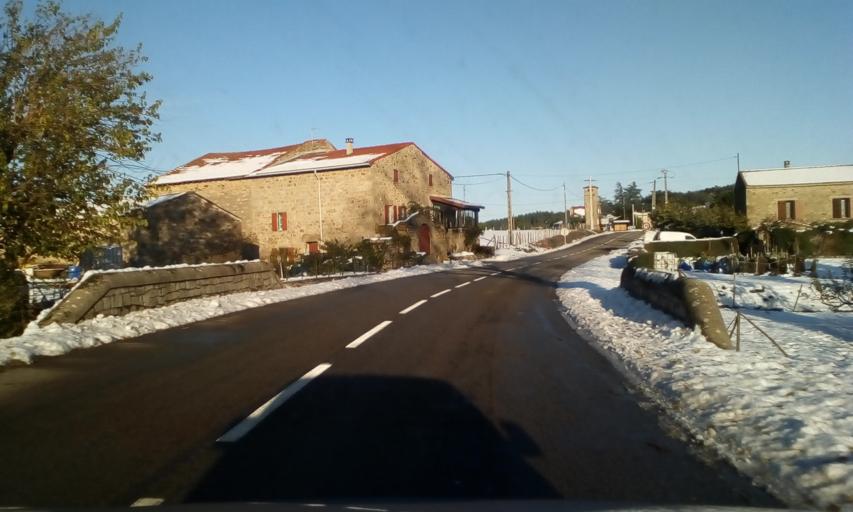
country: FR
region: Rhone-Alpes
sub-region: Departement de l'Ardeche
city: Saint-Felicien
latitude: 45.1119
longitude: 4.6975
